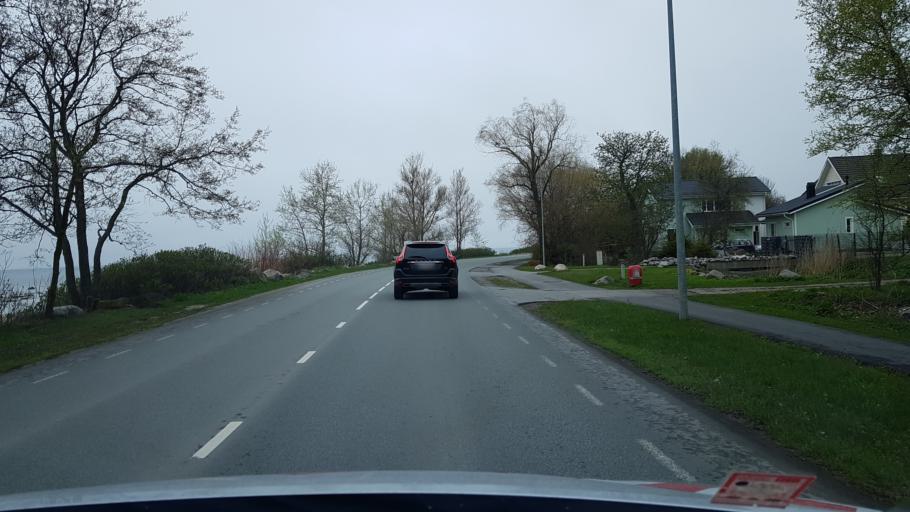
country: EE
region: Harju
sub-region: Viimsi vald
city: Rummu
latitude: 59.5332
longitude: 24.7940
